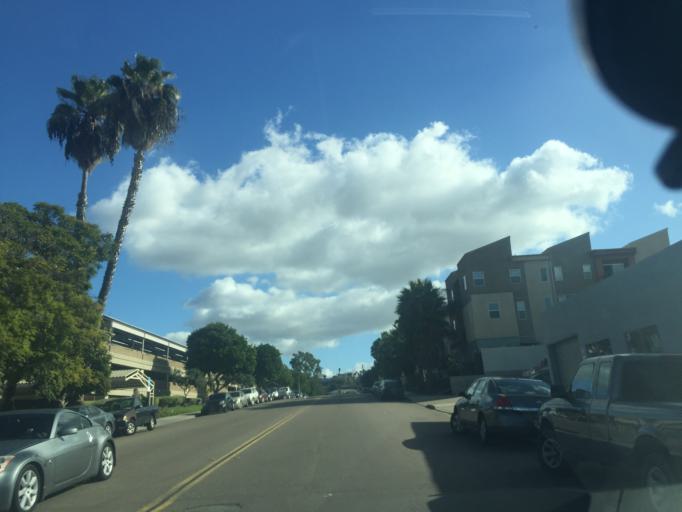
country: US
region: California
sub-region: San Diego County
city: La Mesa
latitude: 32.7898
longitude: -117.0974
